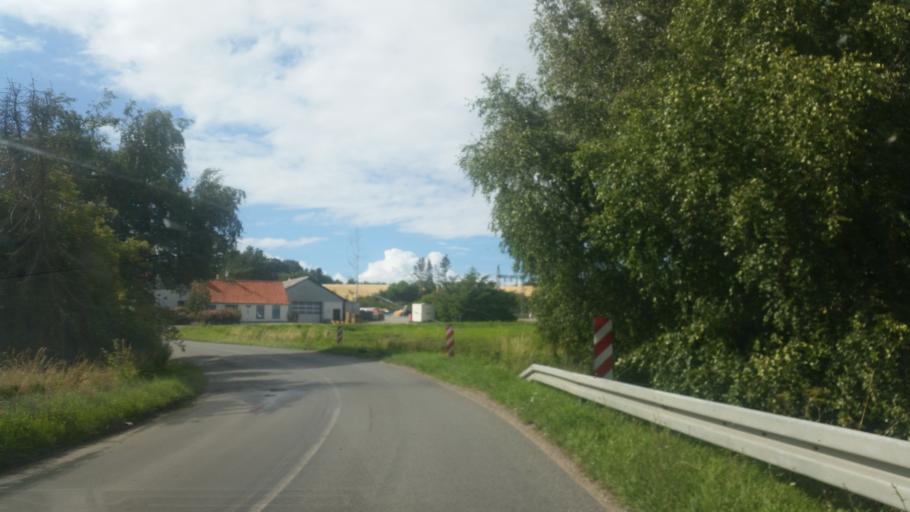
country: DK
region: Zealand
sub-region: Odsherred Kommune
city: Horve
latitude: 55.8121
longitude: 11.4317
